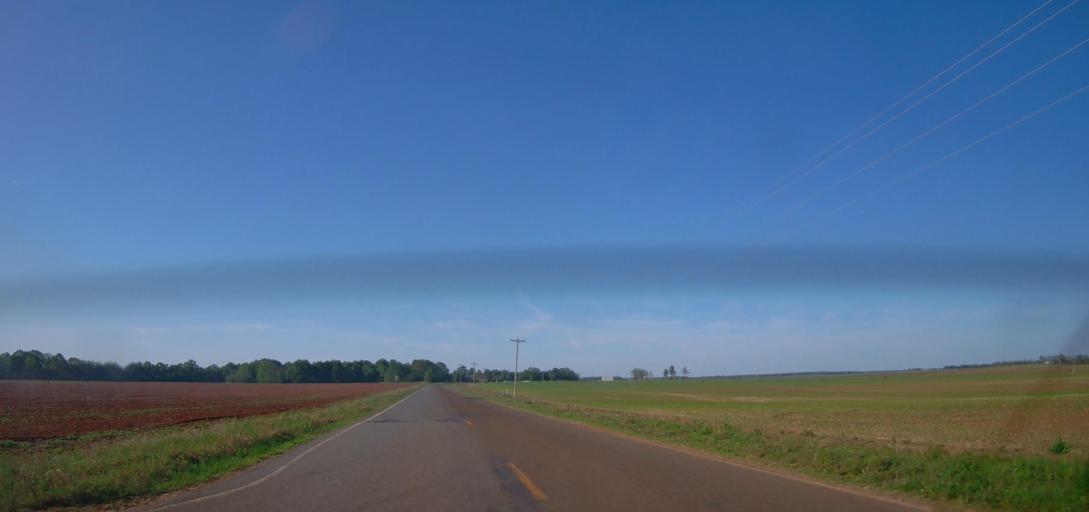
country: US
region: Georgia
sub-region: Macon County
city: Montezuma
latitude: 32.3486
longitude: -83.9437
